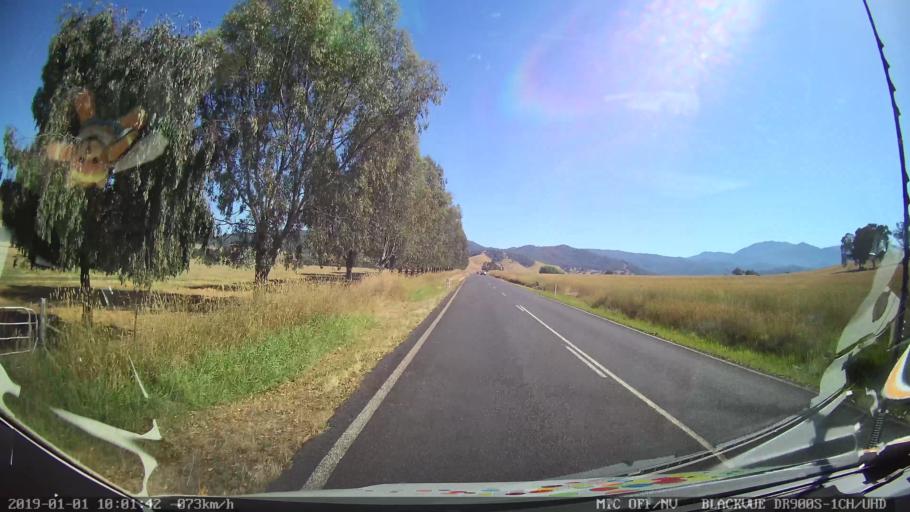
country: AU
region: New South Wales
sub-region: Snowy River
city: Jindabyne
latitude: -36.1888
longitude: 148.1006
